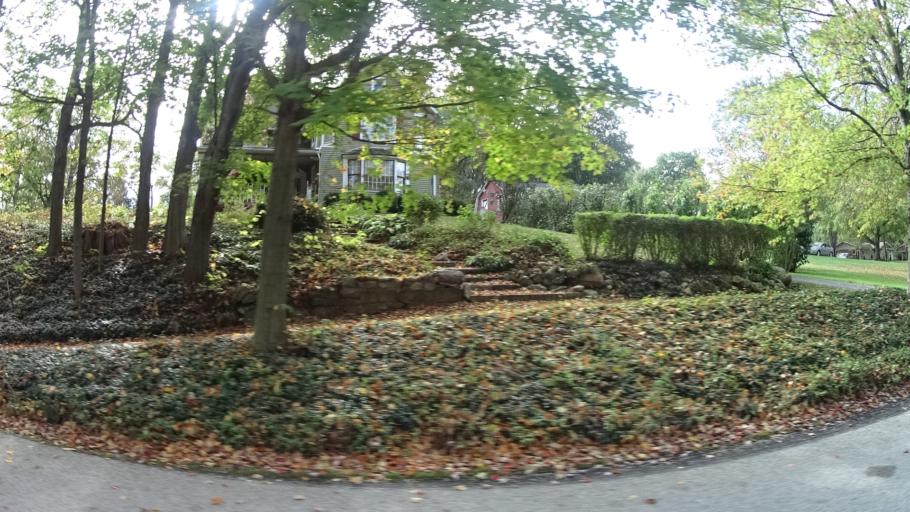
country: US
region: Ohio
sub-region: Lorain County
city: Elyria
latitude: 41.3263
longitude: -82.0740
